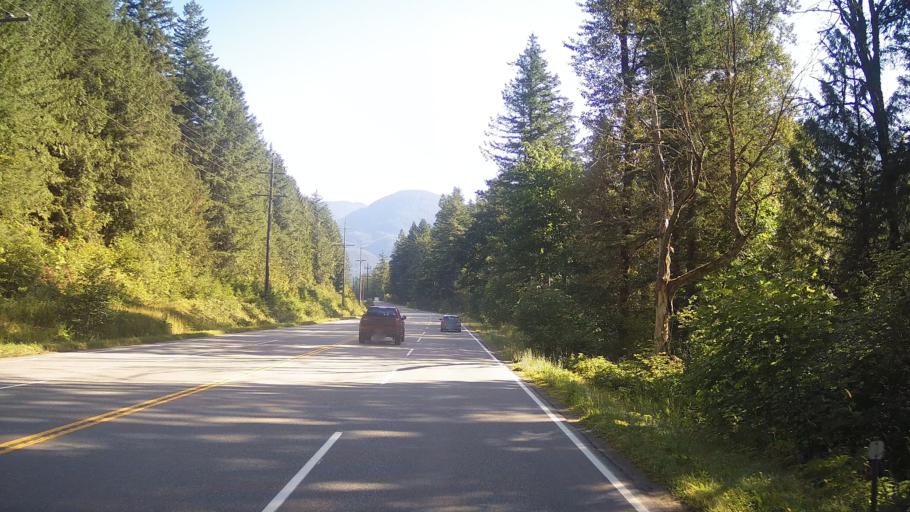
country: CA
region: British Columbia
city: Hope
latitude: 49.4640
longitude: -121.4331
